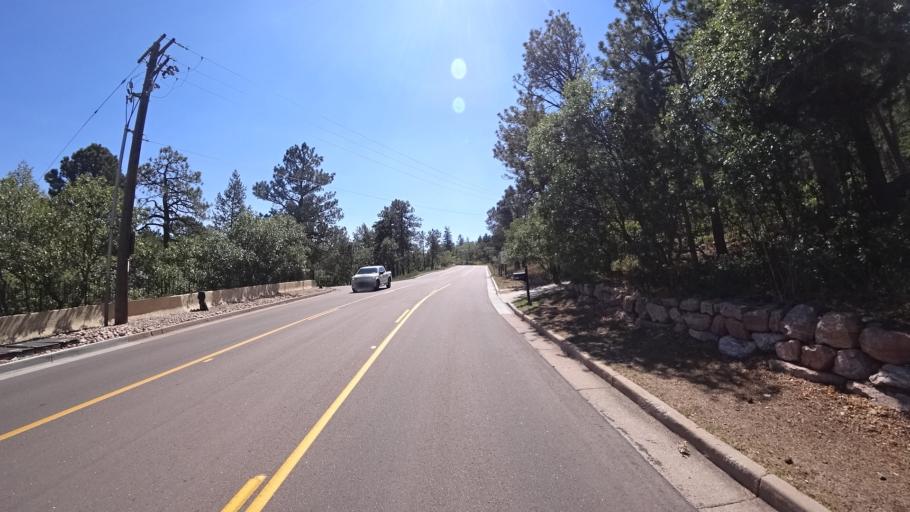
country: US
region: Colorado
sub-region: El Paso County
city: Colorado Springs
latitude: 38.7759
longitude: -104.8553
